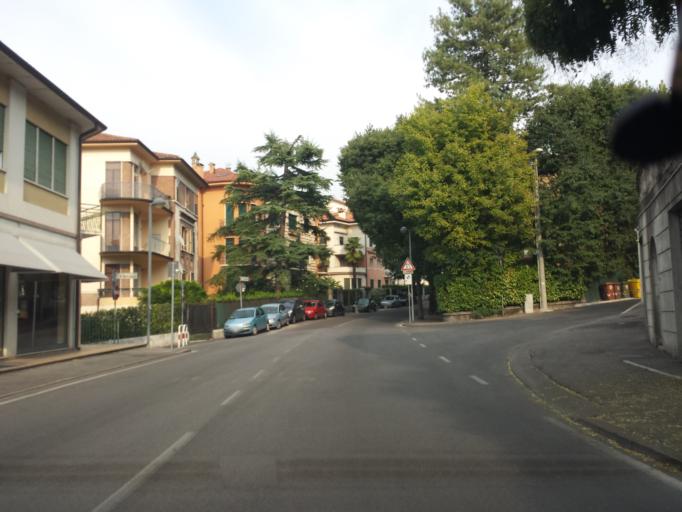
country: IT
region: Veneto
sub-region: Provincia di Vicenza
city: Vicenza
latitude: 45.5404
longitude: 11.5498
